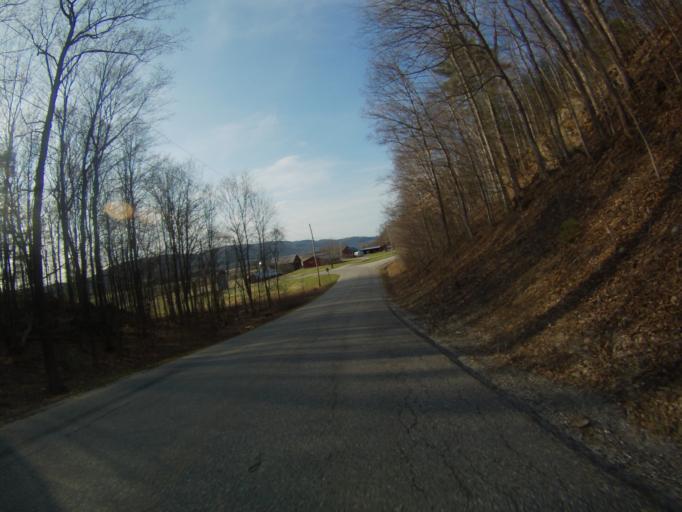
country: US
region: Vermont
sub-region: Addison County
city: Middlebury (village)
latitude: 44.0211
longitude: -73.2239
